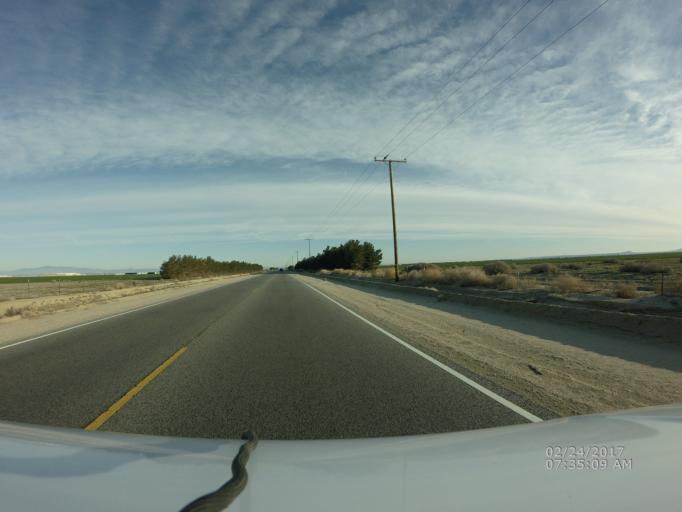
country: US
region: California
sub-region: Los Angeles County
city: Palmdale
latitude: 34.6110
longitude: -118.0409
